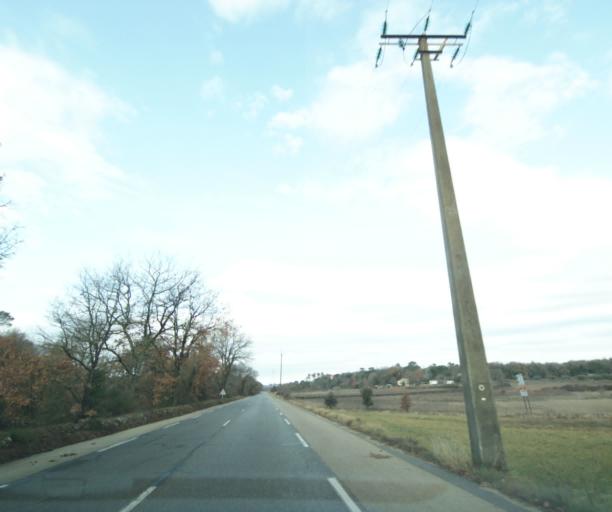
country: FR
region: Provence-Alpes-Cote d'Azur
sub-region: Departement du Var
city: Tourves
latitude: 43.4164
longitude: 5.9151
